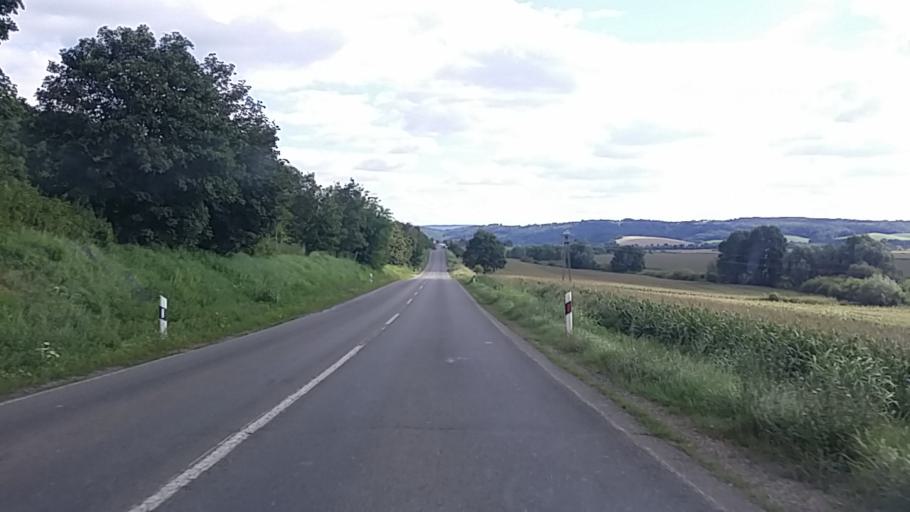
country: HU
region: Baranya
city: Sasd
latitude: 46.2355
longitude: 18.1213
